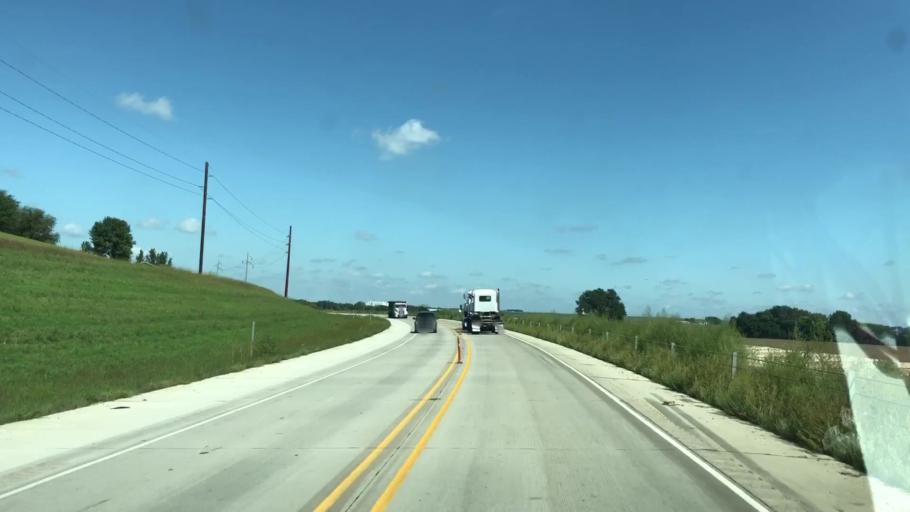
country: US
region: Iowa
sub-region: Plymouth County
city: Le Mars
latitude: 42.7383
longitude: -96.2177
